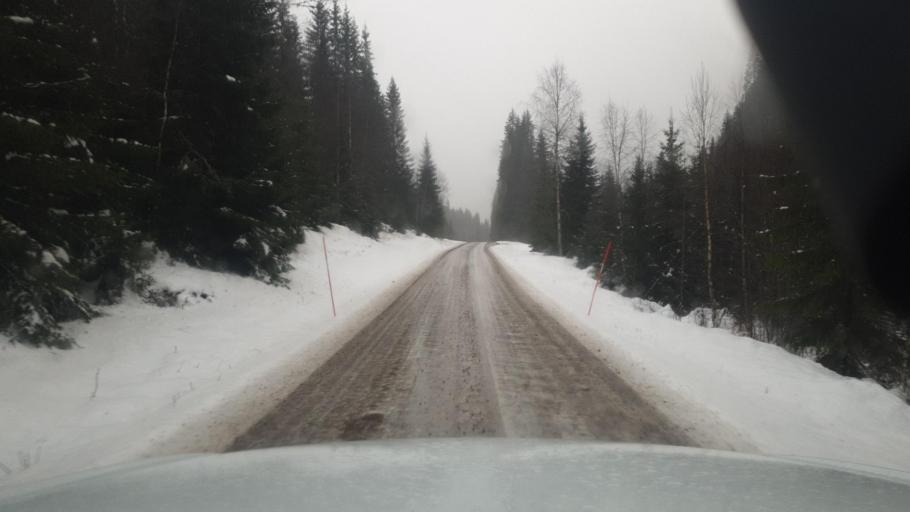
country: SE
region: Vaermland
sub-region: Eda Kommun
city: Charlottenberg
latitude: 60.0393
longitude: 12.5843
